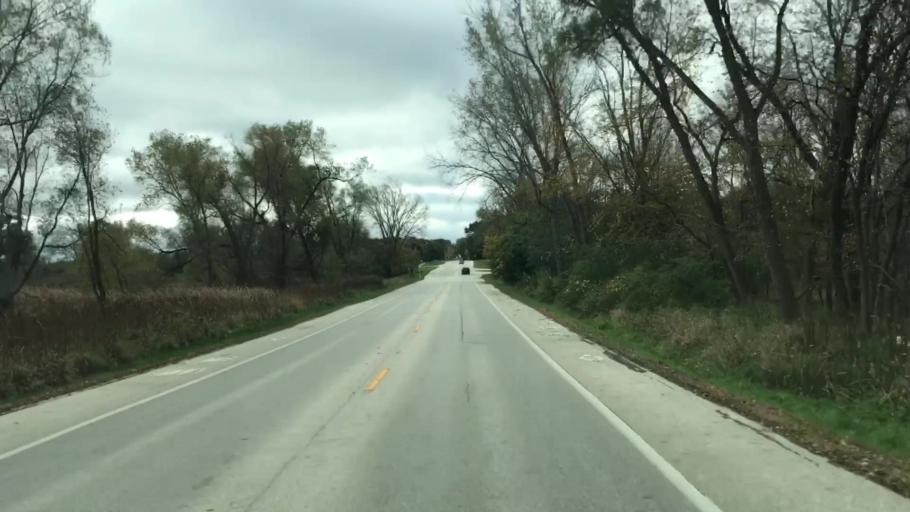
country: US
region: Wisconsin
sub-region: Waukesha County
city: Brookfield
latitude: 43.0740
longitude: -88.1259
